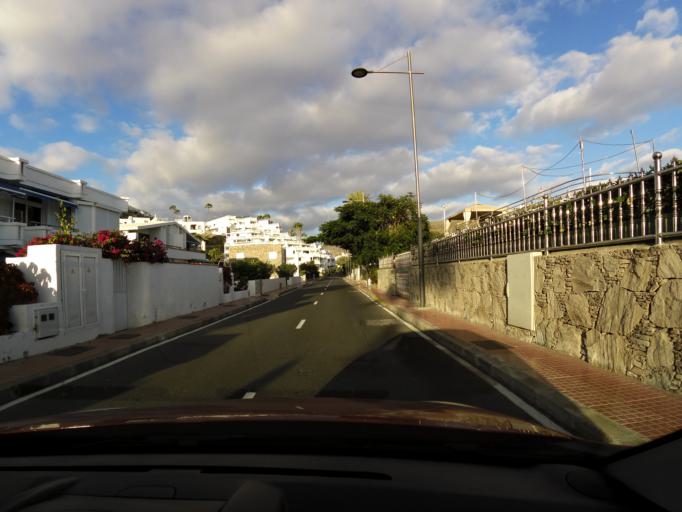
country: ES
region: Canary Islands
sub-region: Provincia de Las Palmas
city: Puerto Rico
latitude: 27.7854
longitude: -15.7140
